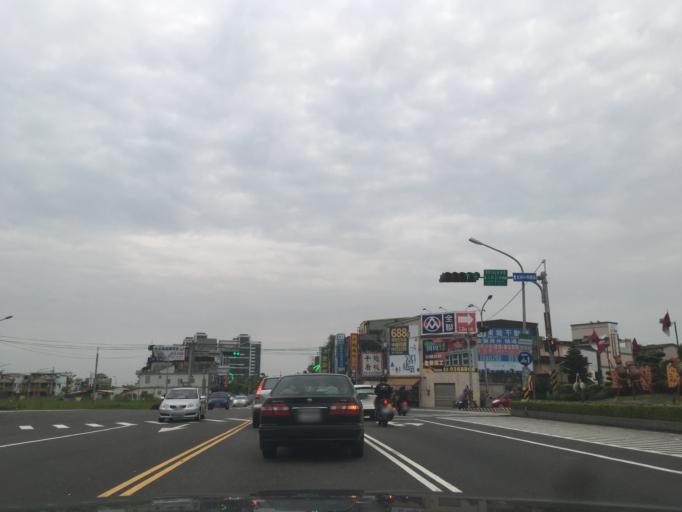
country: TW
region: Taiwan
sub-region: Yilan
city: Yilan
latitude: 24.7437
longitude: 121.7562
